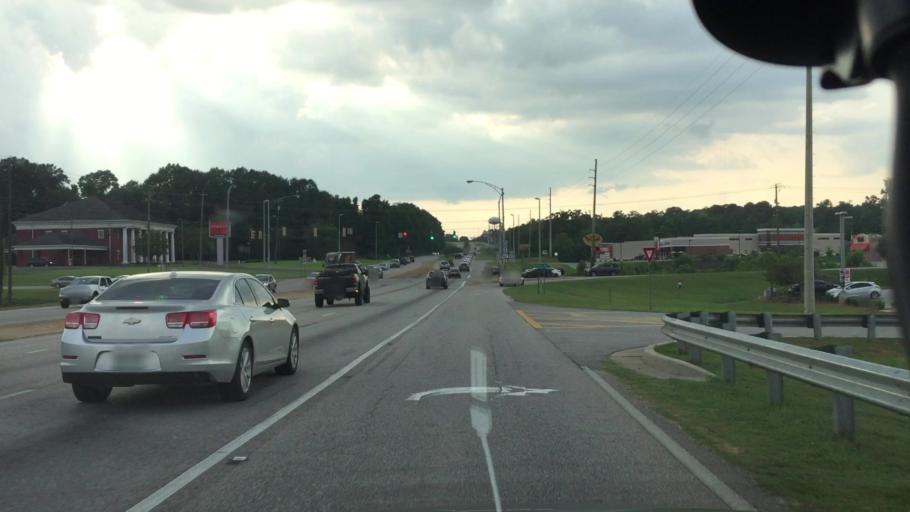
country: US
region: Alabama
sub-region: Coffee County
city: Enterprise
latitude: 31.3284
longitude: -85.8373
